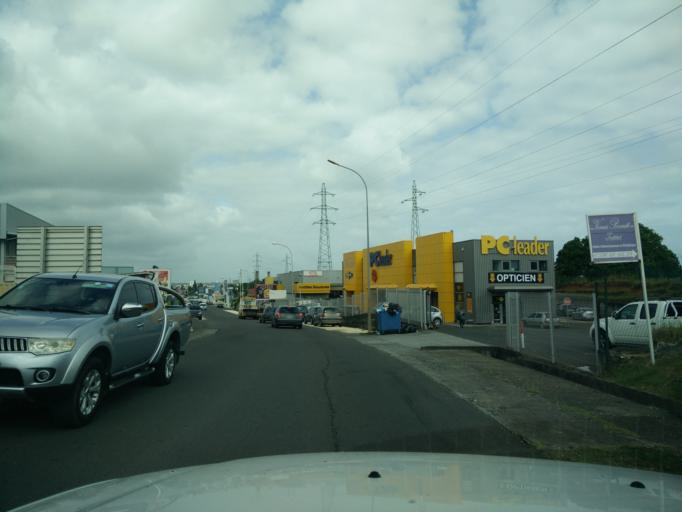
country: GP
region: Guadeloupe
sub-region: Guadeloupe
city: Pointe-a-Pitre
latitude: 16.2375
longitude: -61.5689
